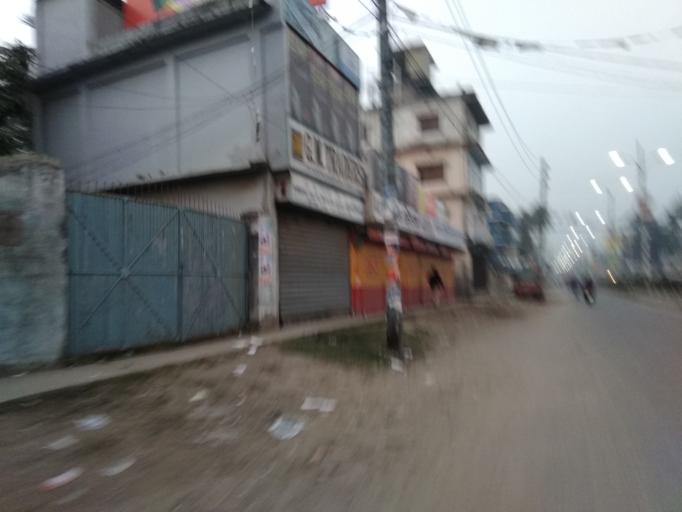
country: BD
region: Rangpur Division
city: Rangpur
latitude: 25.7350
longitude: 89.2547
